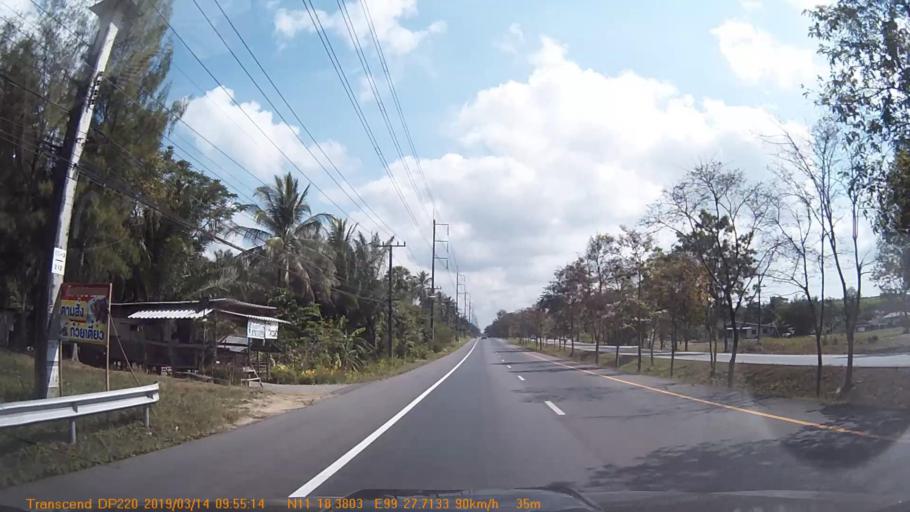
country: TH
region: Prachuap Khiri Khan
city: Bang Saphan
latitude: 11.3066
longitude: 99.4621
